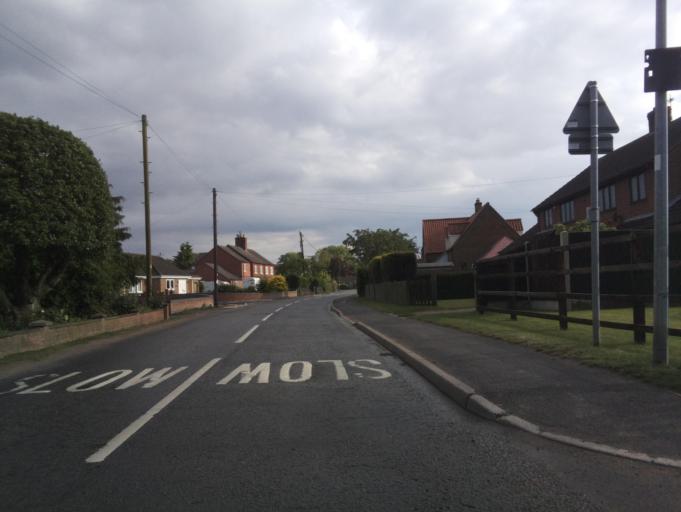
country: GB
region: England
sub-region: Lincolnshire
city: Great Gonerby
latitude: 52.9822
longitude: -0.6741
